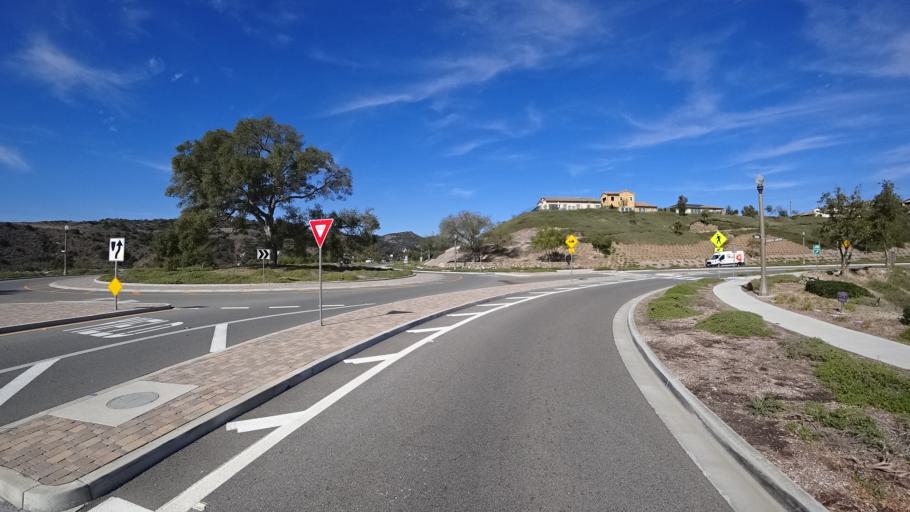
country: US
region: California
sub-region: Orange County
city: Ladera Ranch
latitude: 33.5332
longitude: -117.6073
